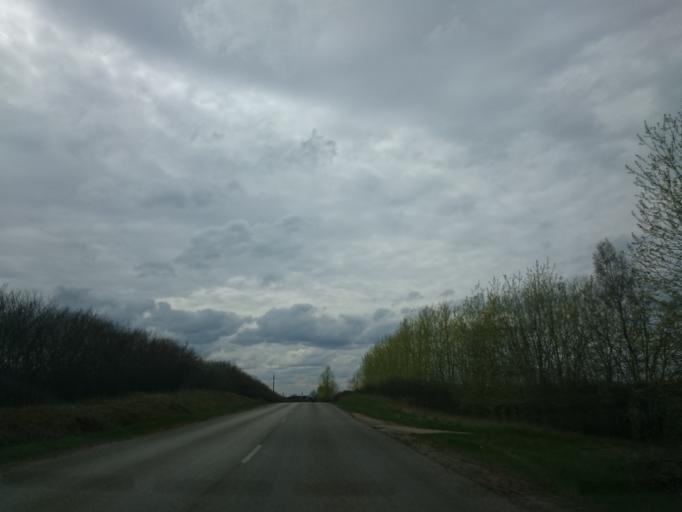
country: LV
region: Tukuma Rajons
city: Tukums
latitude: 56.9300
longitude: 23.0815
